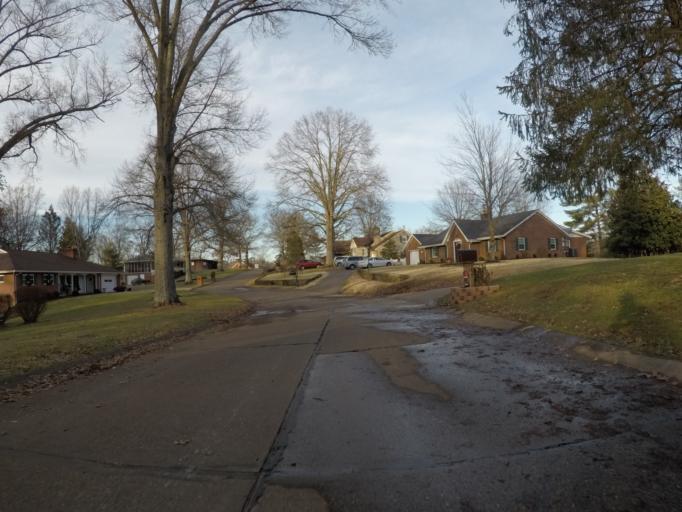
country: US
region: West Virginia
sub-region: Cabell County
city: Huntington
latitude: 38.4051
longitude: -82.3916
